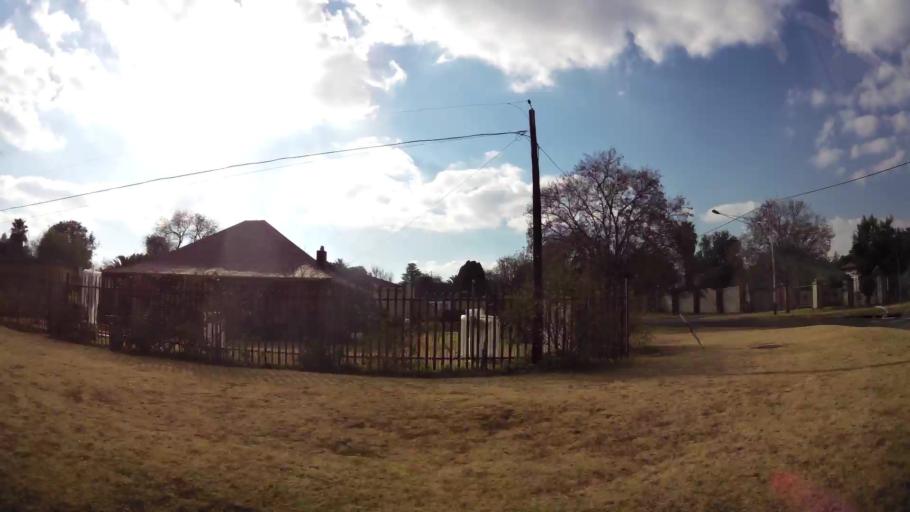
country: ZA
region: Gauteng
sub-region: West Rand District Municipality
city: Krugersdorp
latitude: -26.0886
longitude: 27.7757
